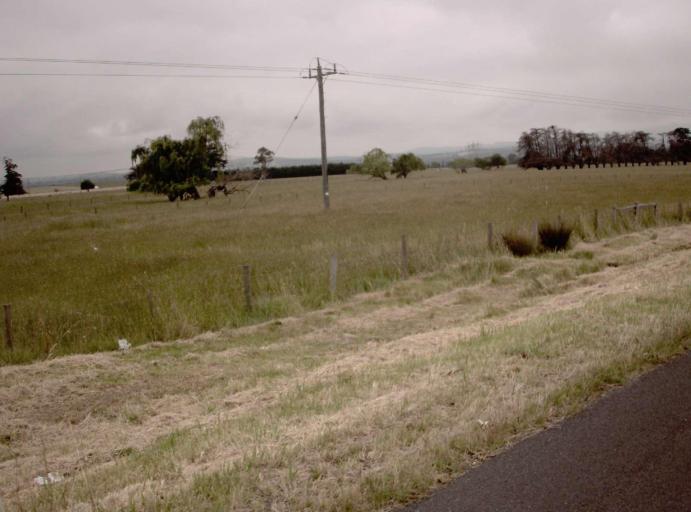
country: AU
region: Victoria
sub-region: Latrobe
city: Morwell
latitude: -38.2670
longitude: 146.4238
